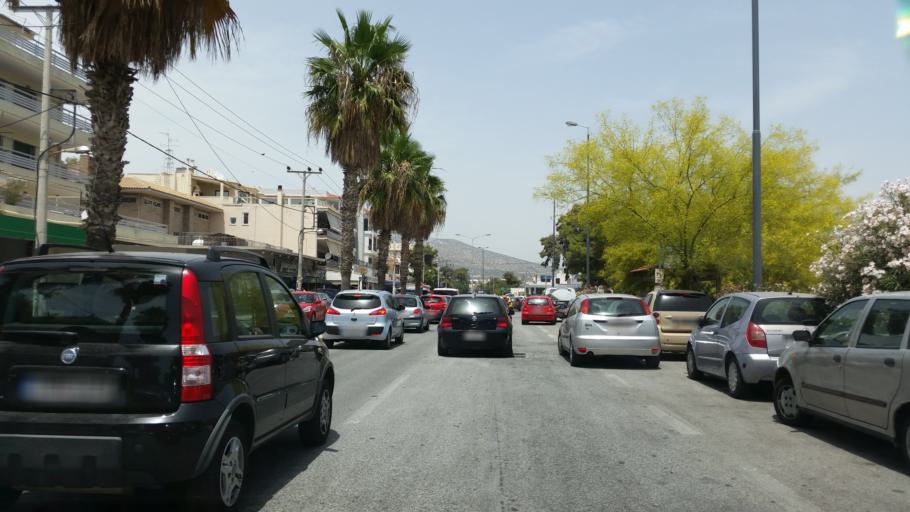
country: GR
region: Attica
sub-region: Nomarchia Anatolikis Attikis
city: Vari
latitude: 37.8198
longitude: 23.8034
